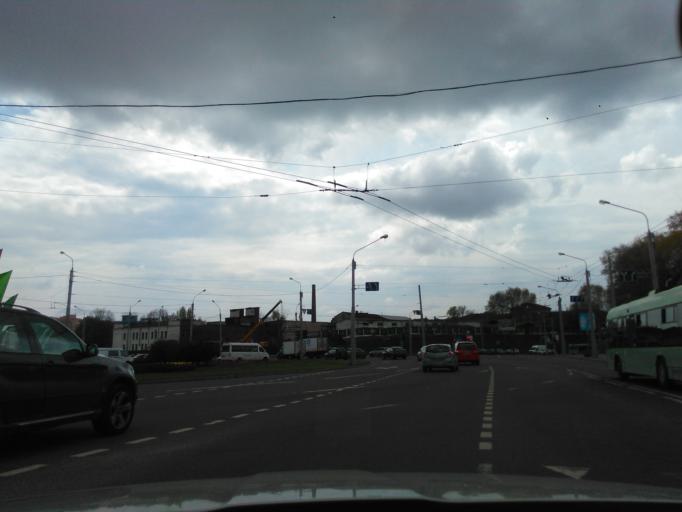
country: BY
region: Minsk
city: Minsk
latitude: 53.8970
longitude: 27.5374
